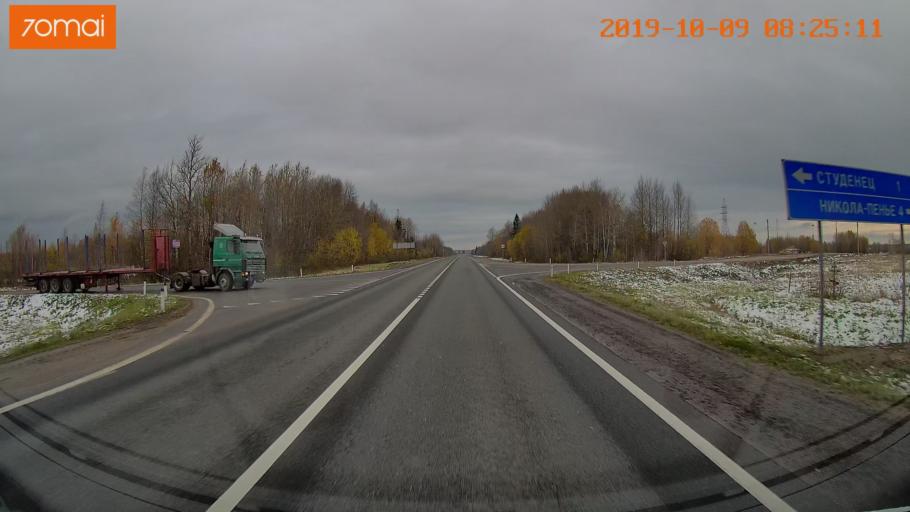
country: RU
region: Vologda
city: Gryazovets
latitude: 58.7772
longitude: 40.2739
